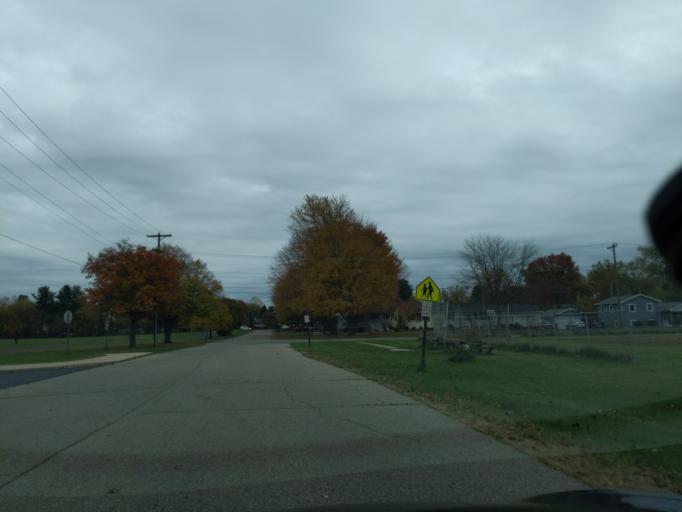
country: US
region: Michigan
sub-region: Eaton County
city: Eaton Rapids
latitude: 42.5153
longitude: -84.6469
